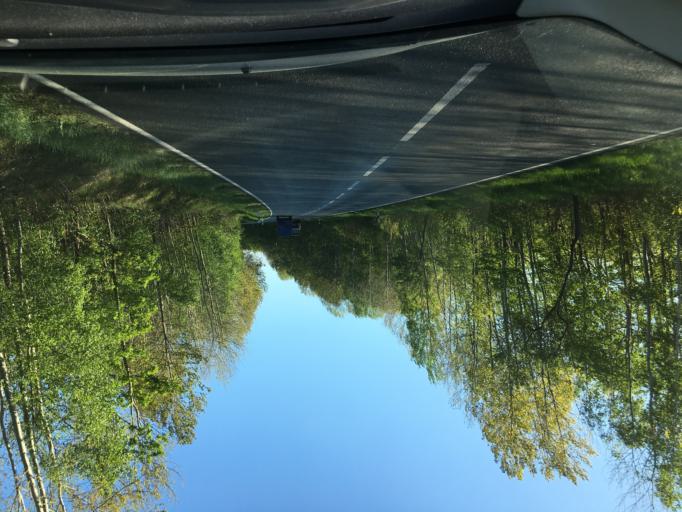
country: DE
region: Saxony
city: Kitzscher
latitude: 51.1299
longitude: 12.5567
